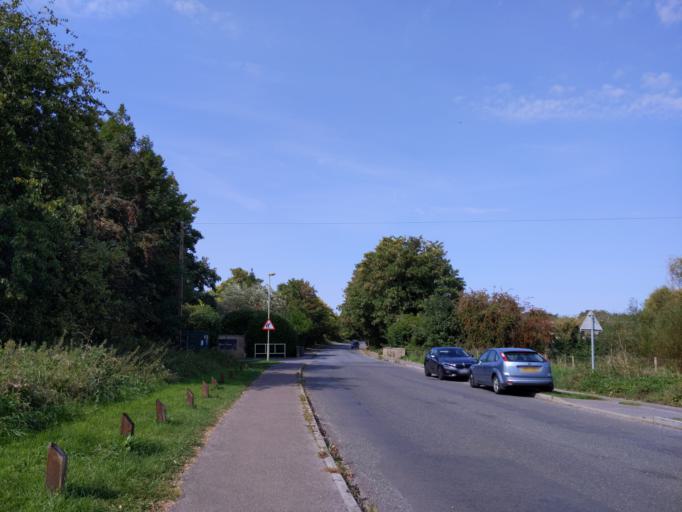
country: GB
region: England
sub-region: Oxfordshire
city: Radley
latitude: 51.7127
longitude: -1.2278
